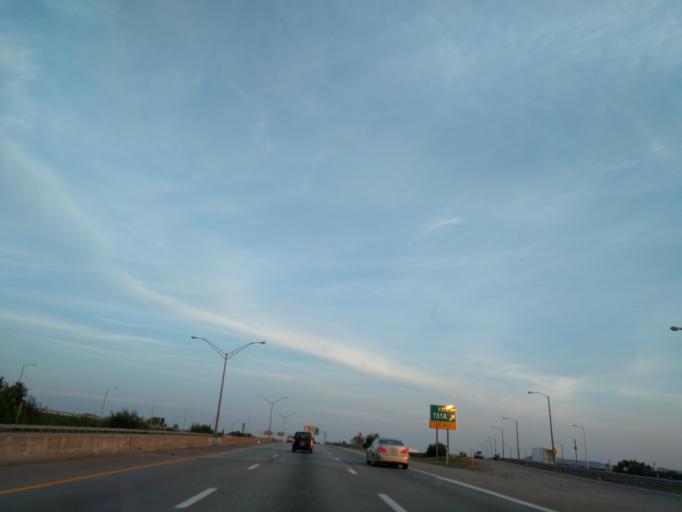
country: US
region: Kentucky
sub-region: Jefferson County
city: Audubon Park
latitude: 38.1922
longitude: -85.7311
